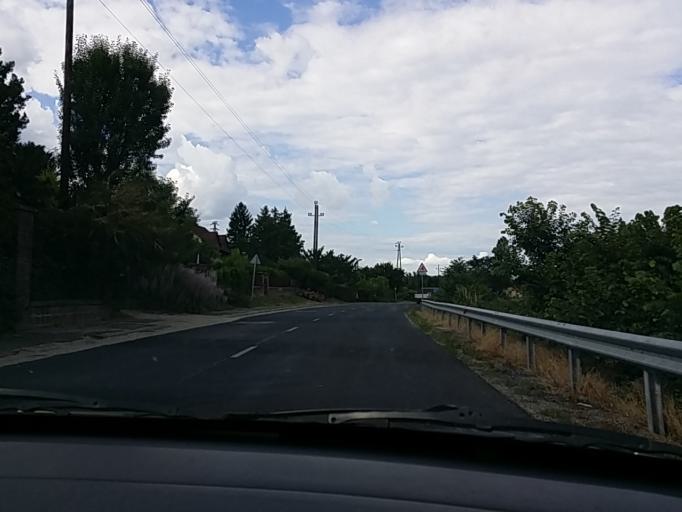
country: HU
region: Veszprem
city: Zanka
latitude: 46.8591
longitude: 17.6702
